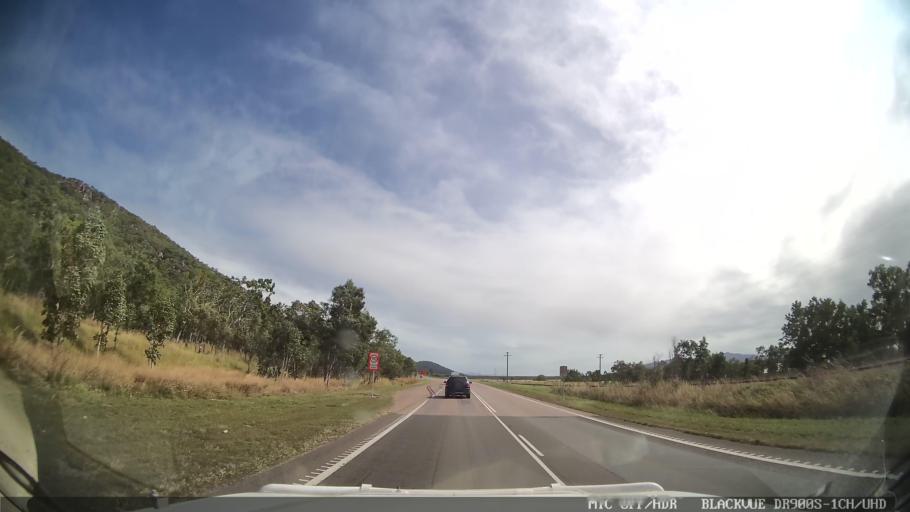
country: AU
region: Queensland
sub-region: Townsville
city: Townsville
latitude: -19.3992
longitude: 147.0242
